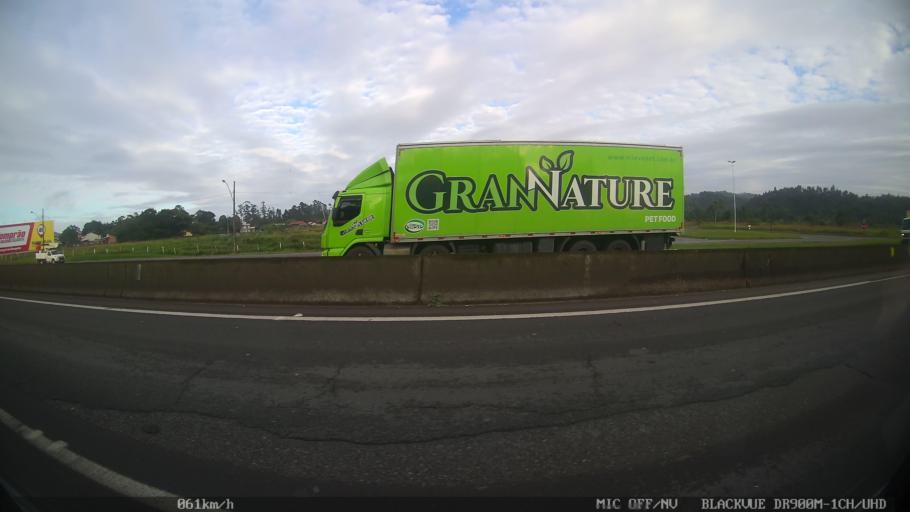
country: BR
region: Santa Catarina
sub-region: Barra Velha
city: Barra Velha
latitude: -26.6184
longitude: -48.7180
